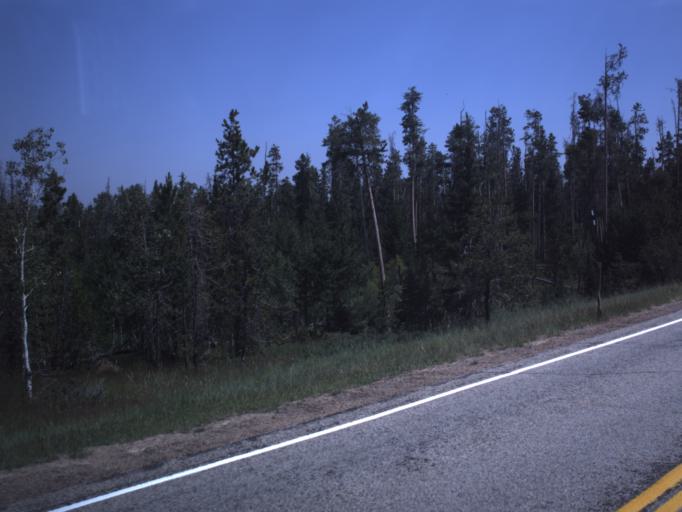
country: US
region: Utah
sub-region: Daggett County
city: Manila
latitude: 40.8552
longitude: -109.5624
